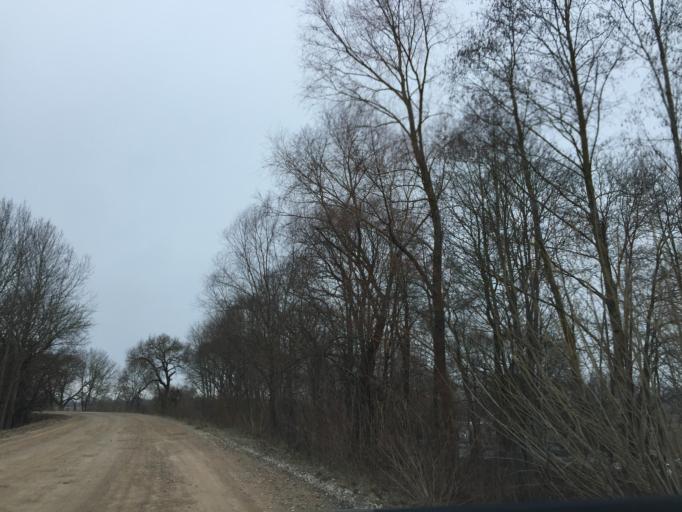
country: LV
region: Ozolnieku
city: Ozolnieki
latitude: 56.6347
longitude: 23.8013
